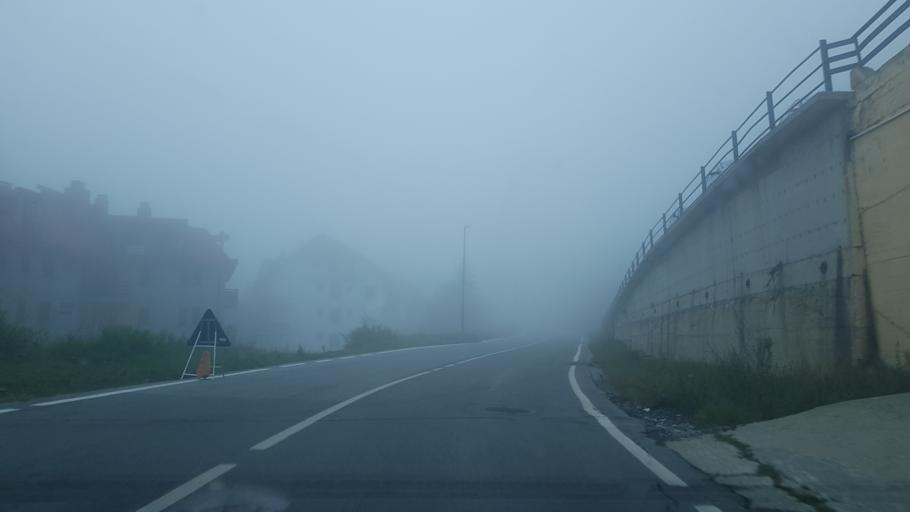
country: IT
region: Piedmont
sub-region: Provincia di Cuneo
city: Frabosa Soprana
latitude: 44.2533
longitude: 7.7913
